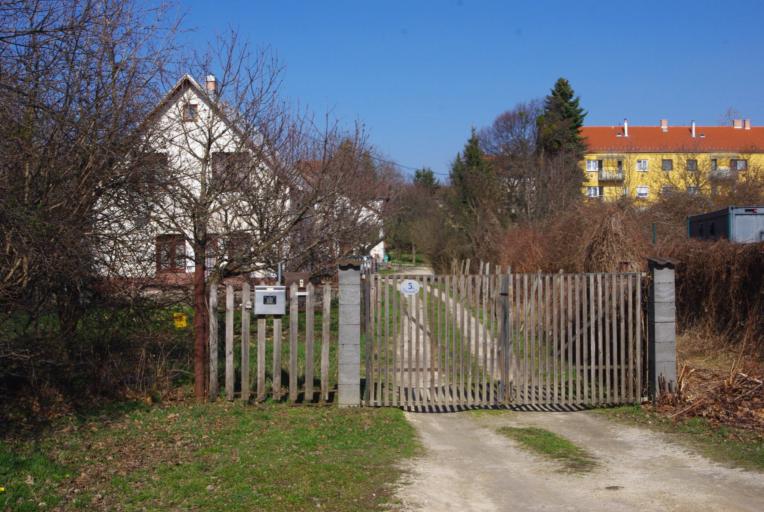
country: HU
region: Pest
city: Budakeszi
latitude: 47.5037
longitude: 18.9184
